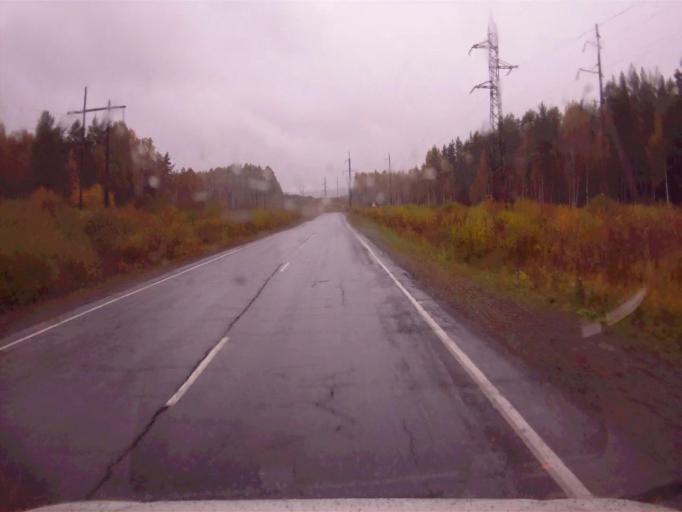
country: RU
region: Chelyabinsk
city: Verkhniy Ufaley
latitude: 55.9472
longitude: 60.4039
